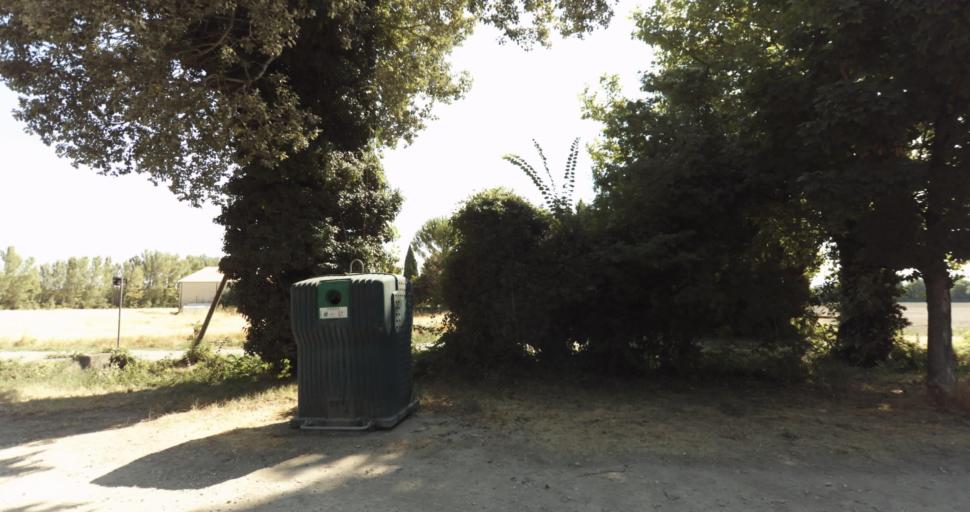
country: FR
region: Provence-Alpes-Cote d'Azur
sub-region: Departement du Vaucluse
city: Althen-des-Paluds
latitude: 44.0047
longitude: 4.9738
